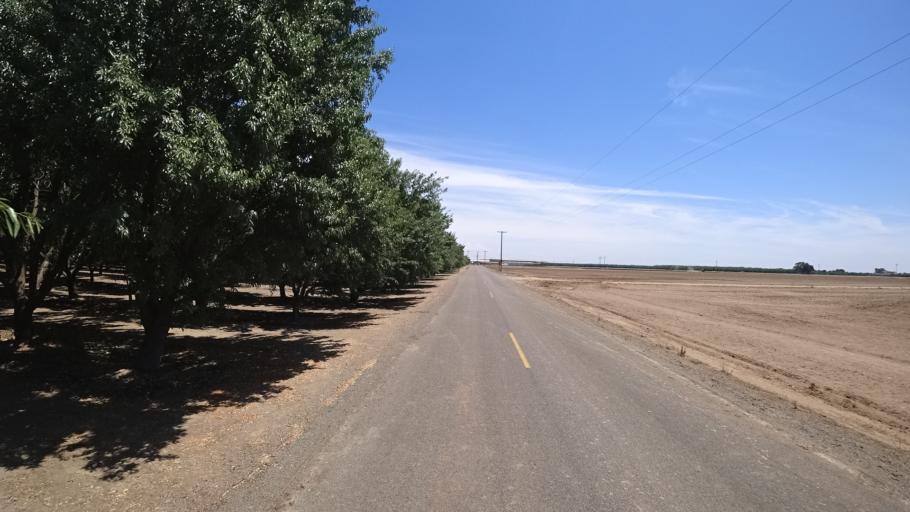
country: US
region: California
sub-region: Kings County
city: Armona
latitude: 36.3390
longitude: -119.7476
